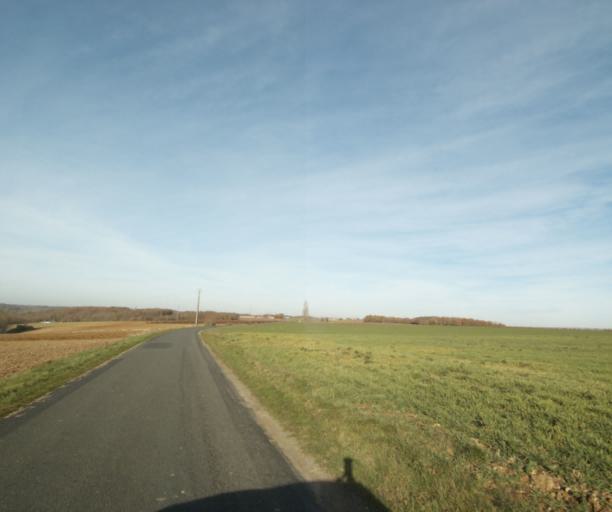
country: FR
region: Poitou-Charentes
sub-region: Departement de la Charente-Maritime
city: Chaniers
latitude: 45.7208
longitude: -0.5288
